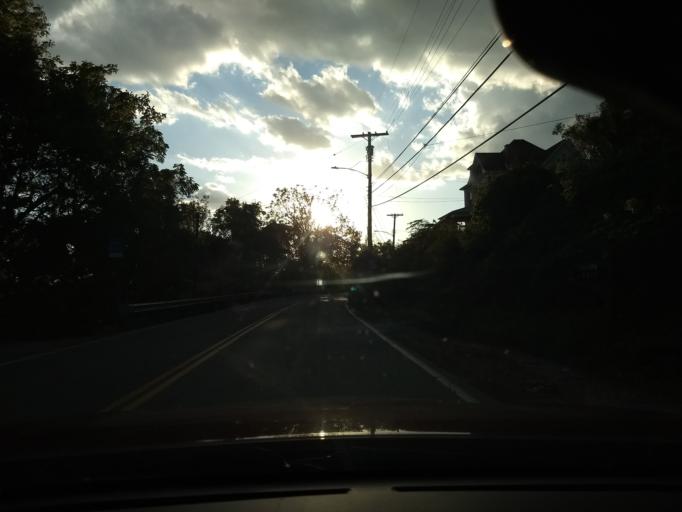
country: US
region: Pennsylvania
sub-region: Allegheny County
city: Dravosburg
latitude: 40.3524
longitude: -79.9031
